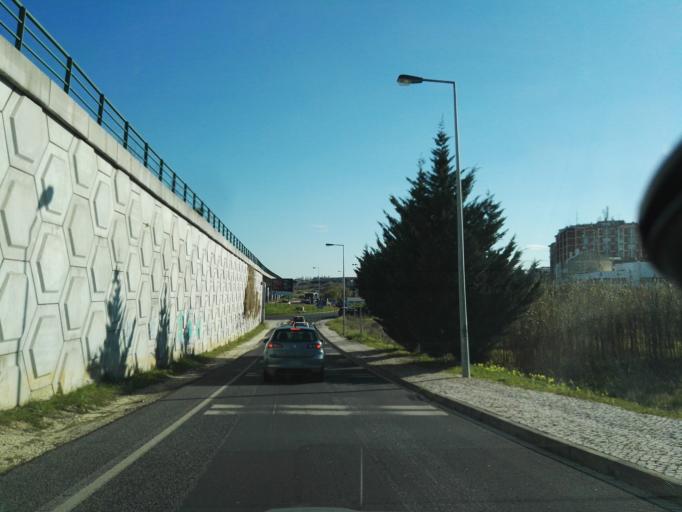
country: PT
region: Setubal
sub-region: Seixal
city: Corroios
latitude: 38.6430
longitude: -9.1495
